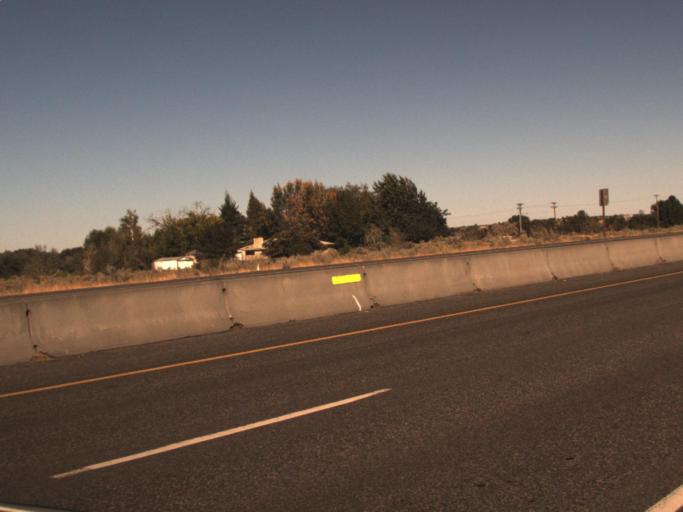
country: US
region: Washington
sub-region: Benton County
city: Richland
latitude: 46.2873
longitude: -119.3064
